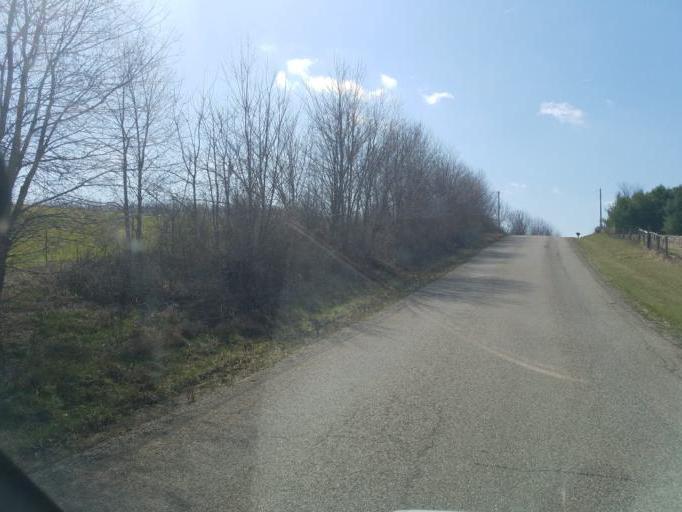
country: US
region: Ohio
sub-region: Licking County
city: Utica
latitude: 40.2516
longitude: -82.3374
